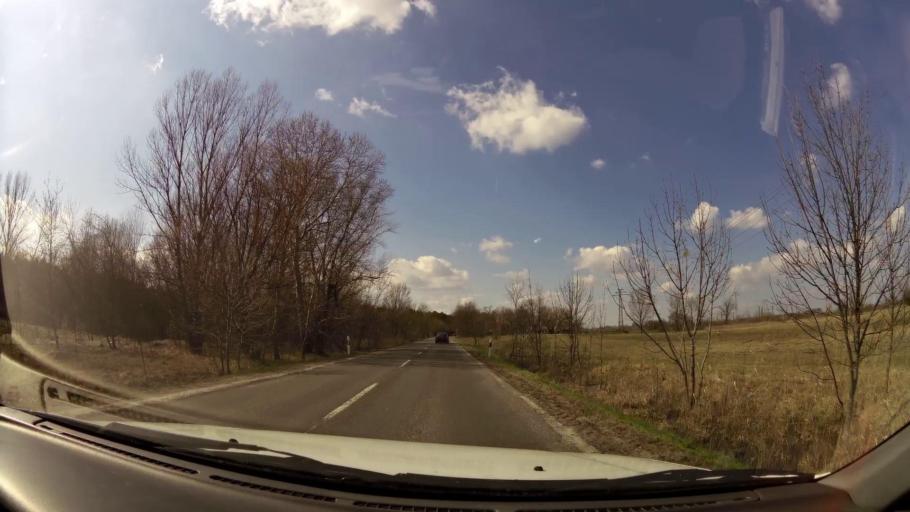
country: HU
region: Pest
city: Farmos
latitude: 47.3580
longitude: 19.8207
